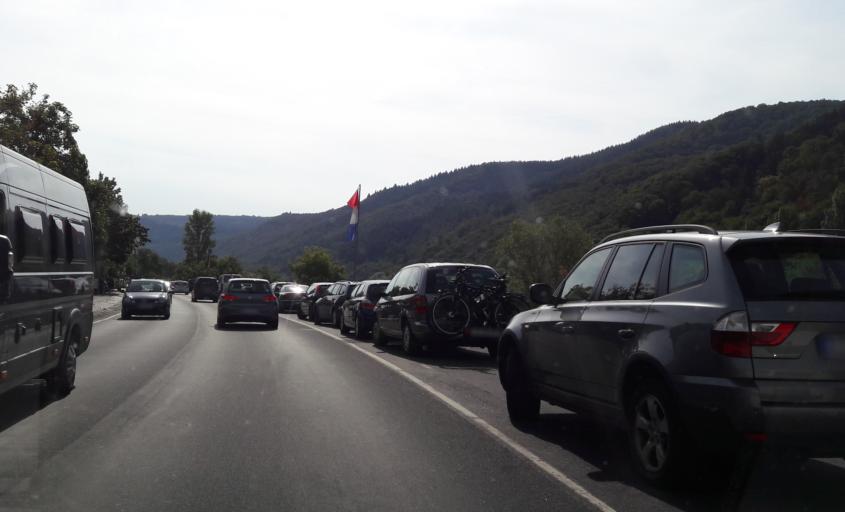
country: DE
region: Rheinland-Pfalz
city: Ediger-Eller
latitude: 50.0949
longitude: 7.1559
